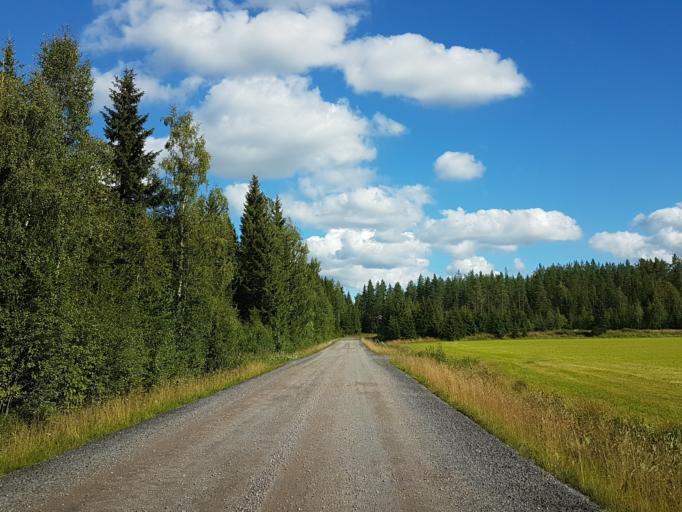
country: SE
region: Vaesterbotten
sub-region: Skelleftea Kommun
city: Burtraesk
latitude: 64.2950
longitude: 20.5025
